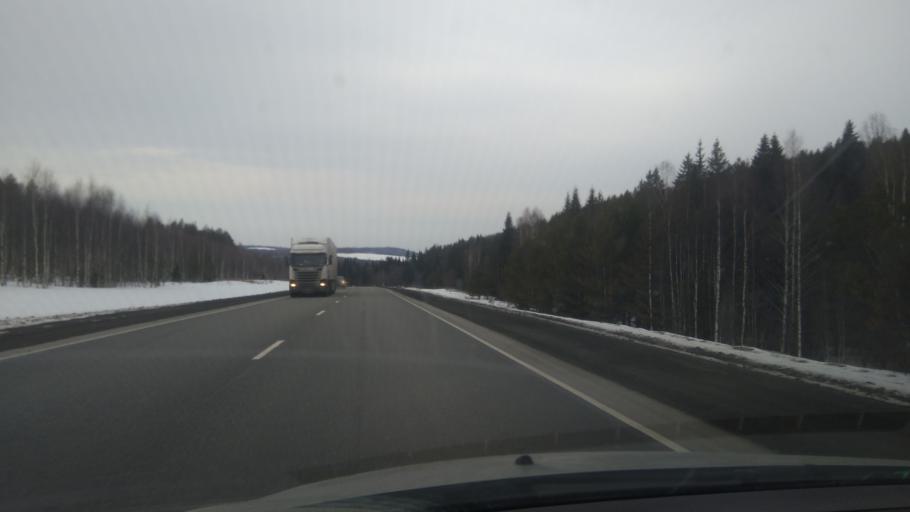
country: RU
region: Sverdlovsk
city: Arti
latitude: 56.7968
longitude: 58.6405
